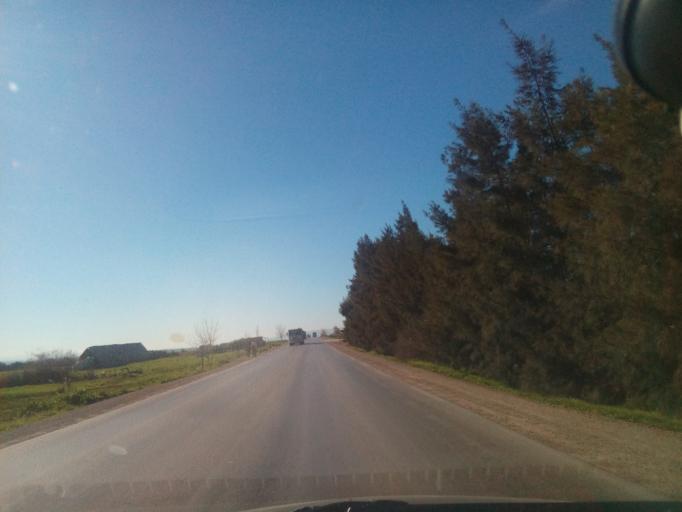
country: DZ
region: Relizane
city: Djidiouia
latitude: 35.8983
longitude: 0.6812
